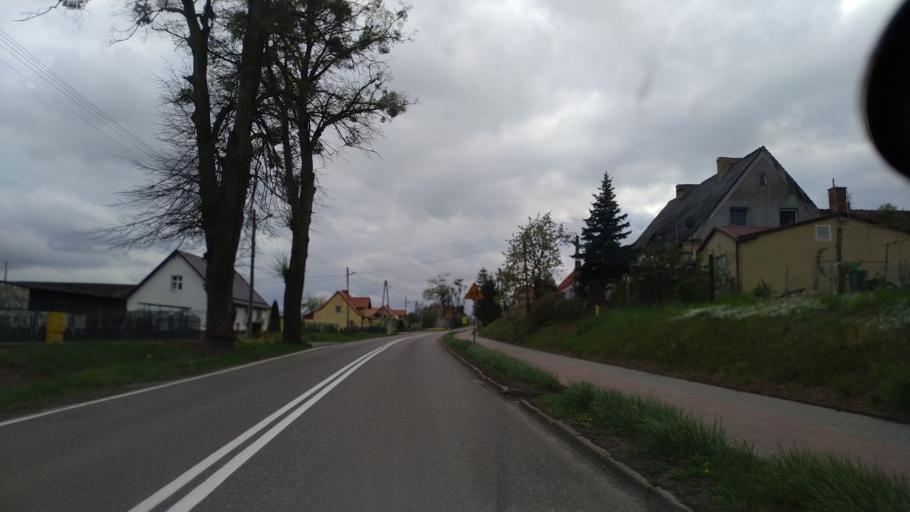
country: PL
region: Pomeranian Voivodeship
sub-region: Powiat kwidzynski
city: Ryjewo
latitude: 53.7866
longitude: 18.9639
